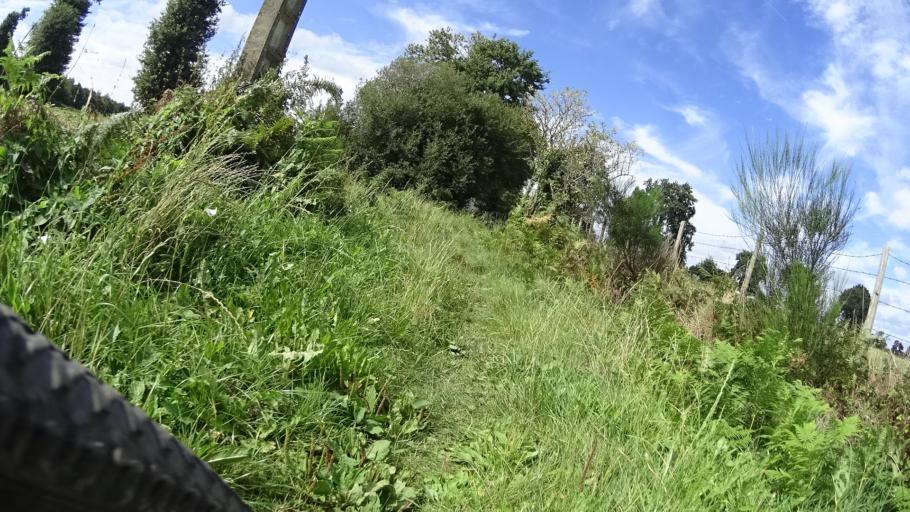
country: FR
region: Brittany
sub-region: Departement d'Ille-et-Vilaine
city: La Meziere
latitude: 48.2194
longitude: -1.7373
